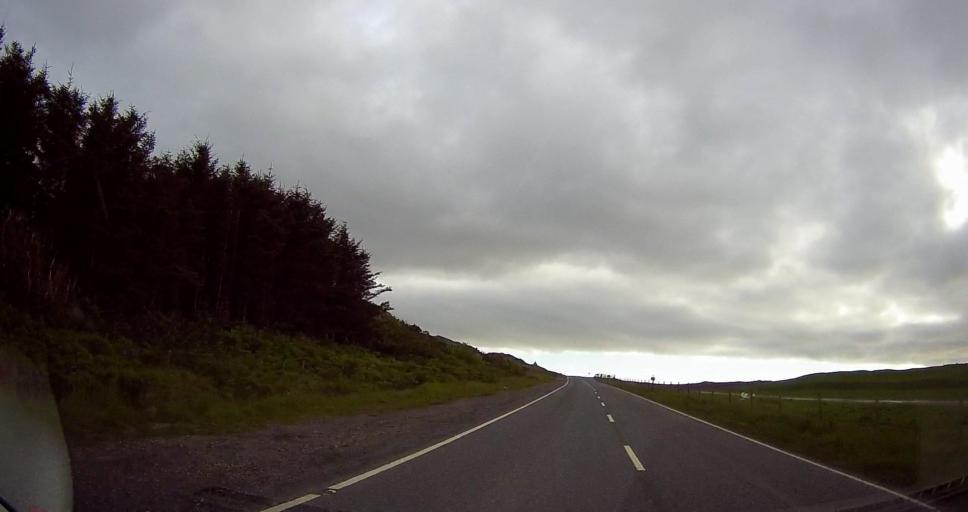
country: GB
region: Scotland
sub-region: Shetland Islands
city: Lerwick
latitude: 60.4315
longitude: -1.2960
